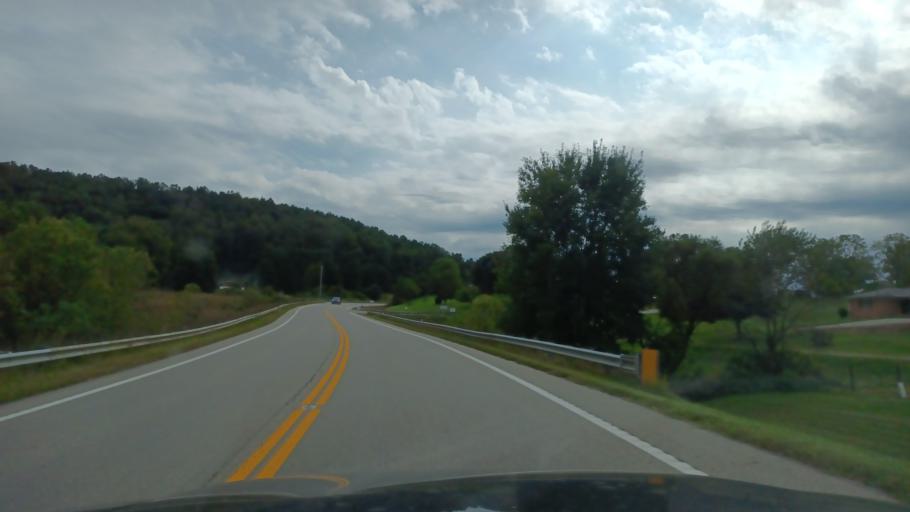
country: US
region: Ohio
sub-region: Vinton County
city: McArthur
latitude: 39.2640
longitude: -82.6810
